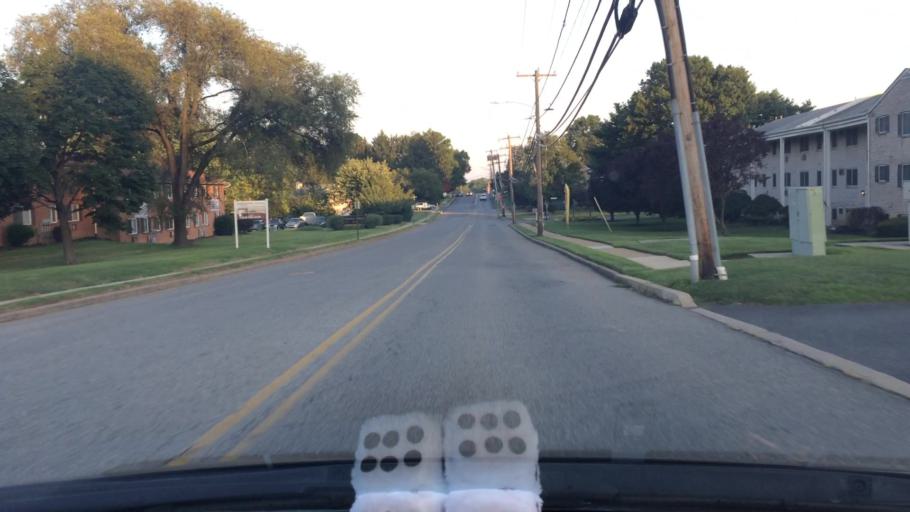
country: US
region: Pennsylvania
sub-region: Delaware County
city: Village Green-Green Ridge
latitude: 39.8559
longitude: -75.4443
